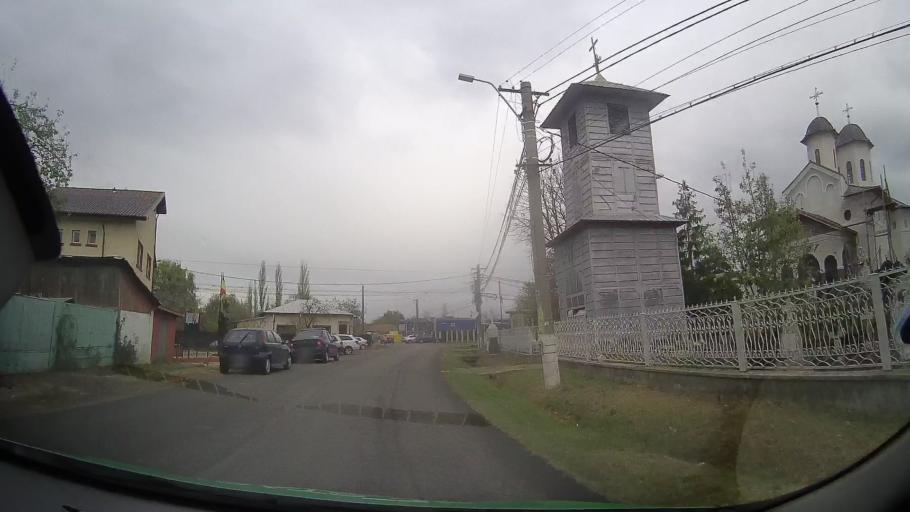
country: RO
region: Prahova
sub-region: Comuna Colceag
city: Inotesti
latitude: 44.9604
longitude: 26.3580
